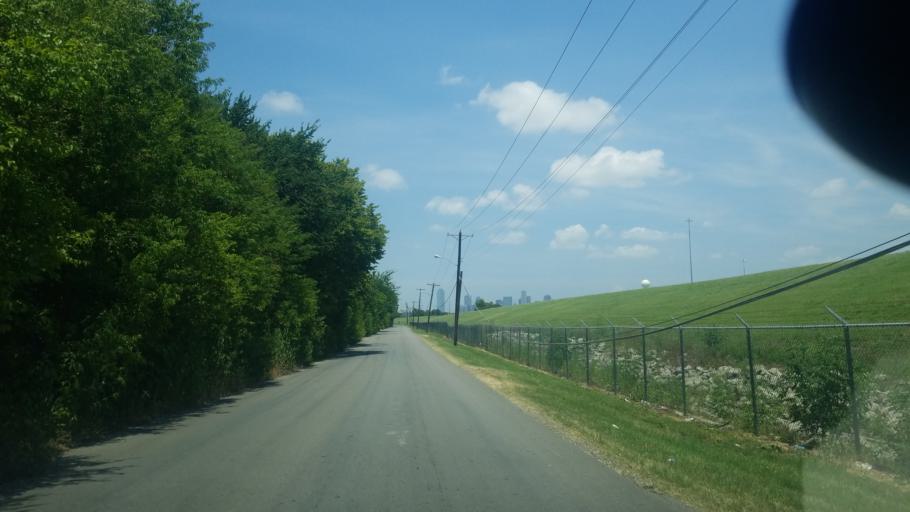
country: US
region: Texas
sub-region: Dallas County
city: Dallas
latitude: 32.7301
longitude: -96.7742
